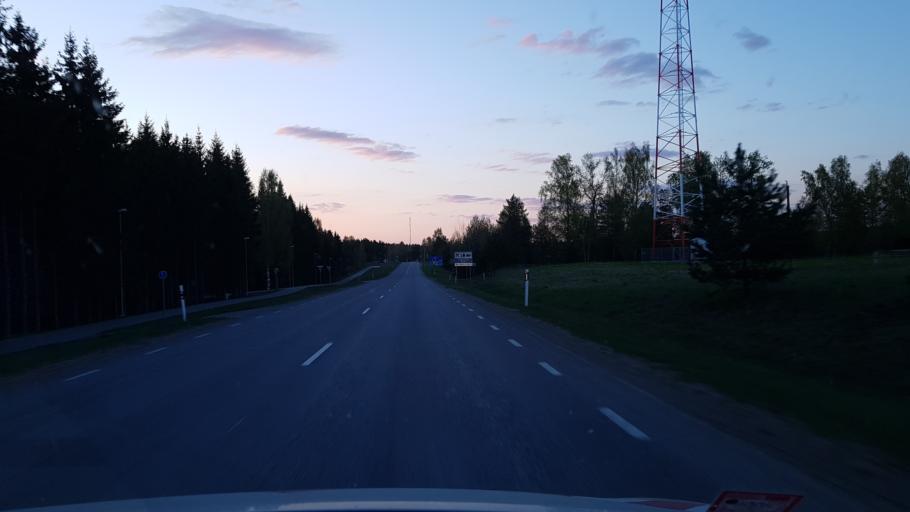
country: EE
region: Vorumaa
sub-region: Voru linn
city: Voru
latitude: 57.8112
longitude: 27.0314
